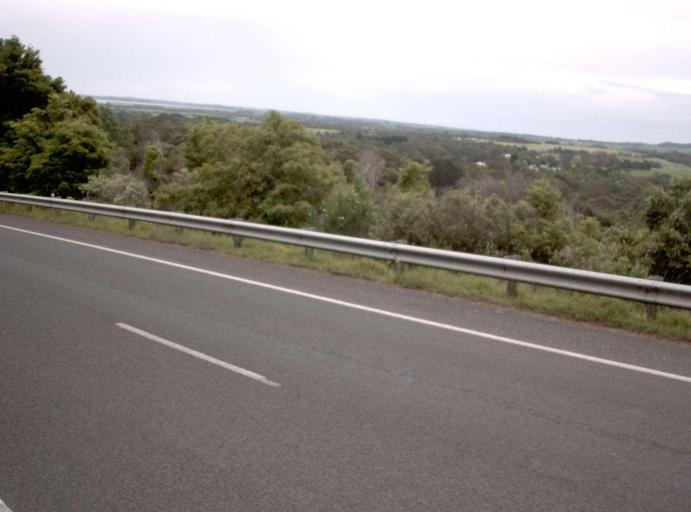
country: AU
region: Victoria
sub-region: Latrobe
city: Morwell
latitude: -38.6409
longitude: 146.2018
